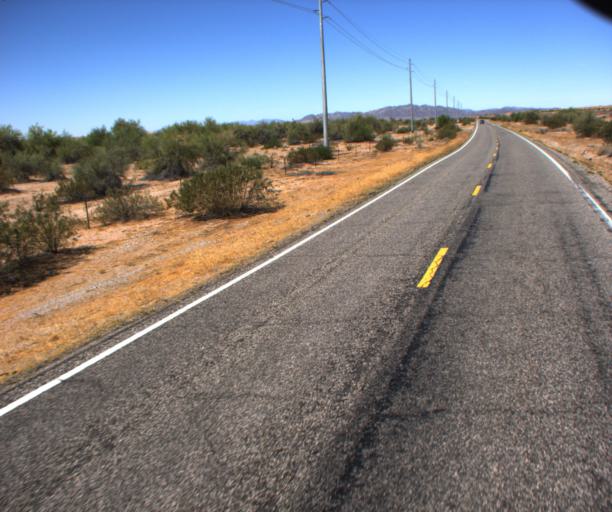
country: US
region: Arizona
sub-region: La Paz County
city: Cienega Springs
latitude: 33.9942
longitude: -114.1364
